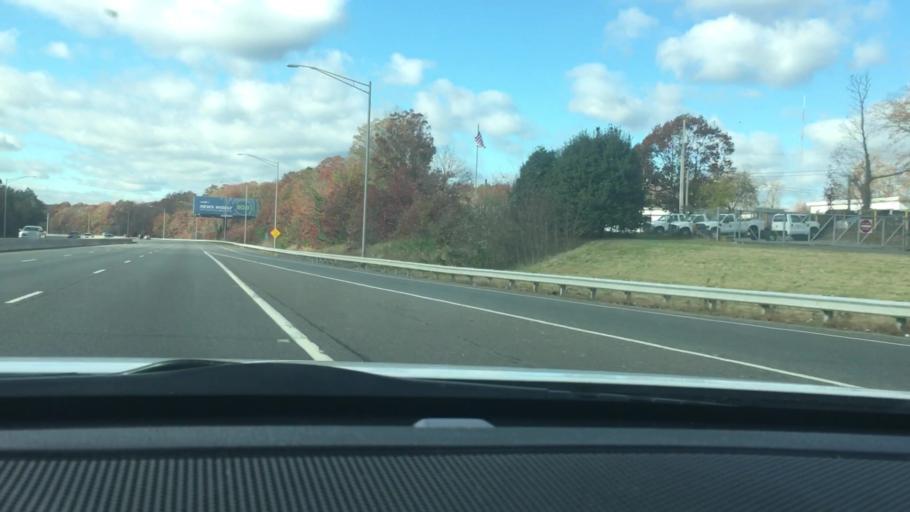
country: US
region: New Jersey
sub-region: Atlantic County
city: Pleasantville
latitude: 39.4039
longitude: -74.5273
